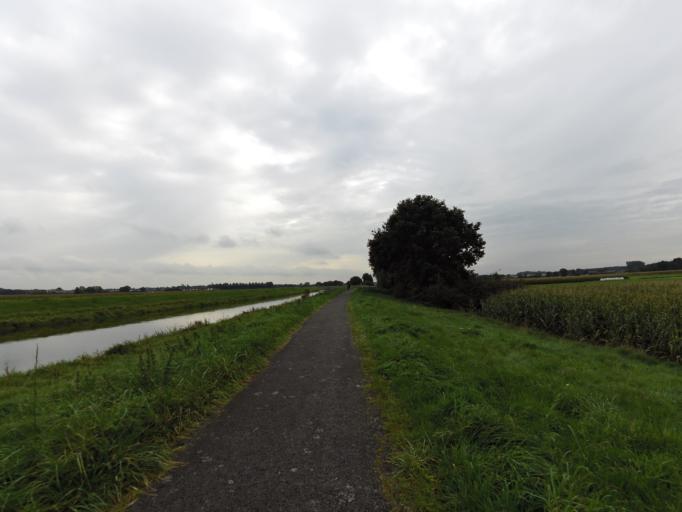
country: DE
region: North Rhine-Westphalia
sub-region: Regierungsbezirk Munster
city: Isselburg
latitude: 51.8627
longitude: 6.4537
